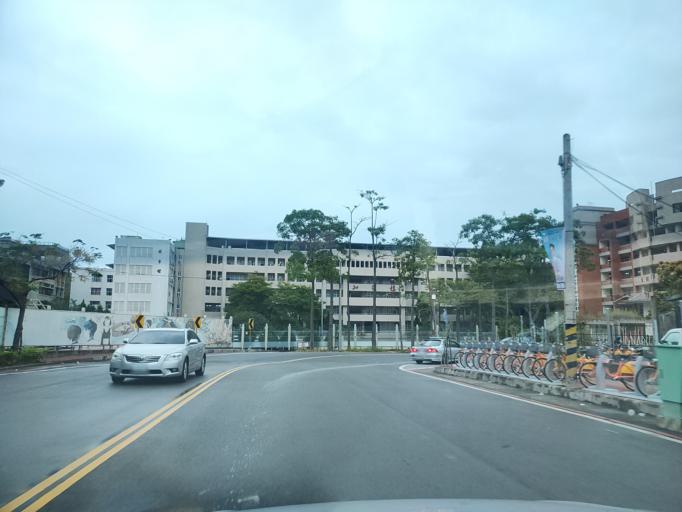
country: TW
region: Taiwan
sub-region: Miaoli
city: Miaoli
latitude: 24.5582
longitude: 120.8164
